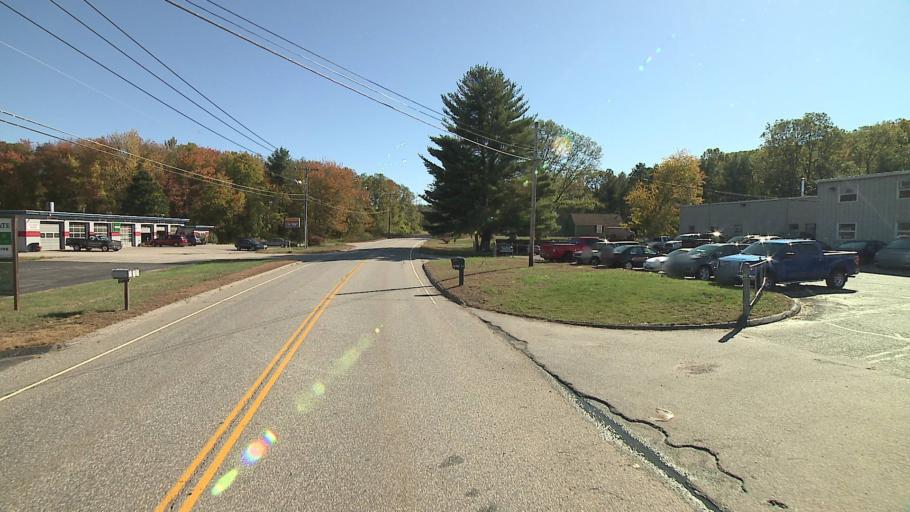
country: US
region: Connecticut
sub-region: Tolland County
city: South Coventry
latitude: 41.7198
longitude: -72.2724
